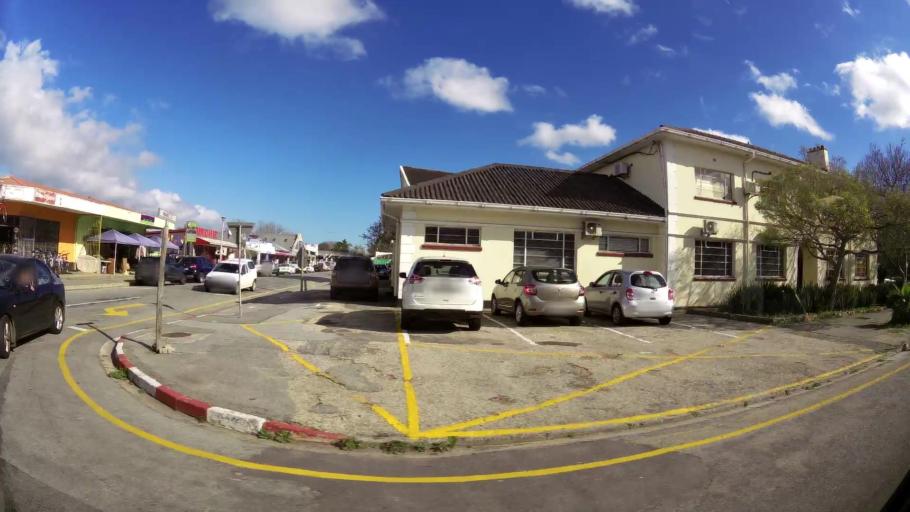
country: ZA
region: Western Cape
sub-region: Eden District Municipality
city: Knysna
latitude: -34.0378
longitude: 23.0504
